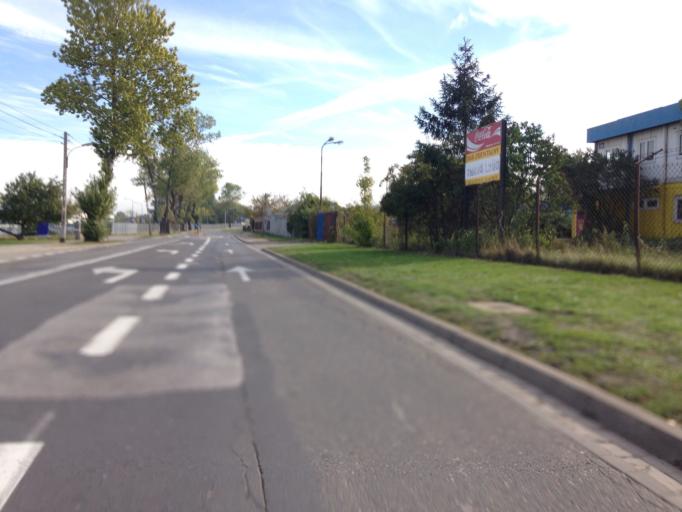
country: PL
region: Masovian Voivodeship
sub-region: Warszawa
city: Praga Poludnie
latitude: 52.2607
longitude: 21.0717
